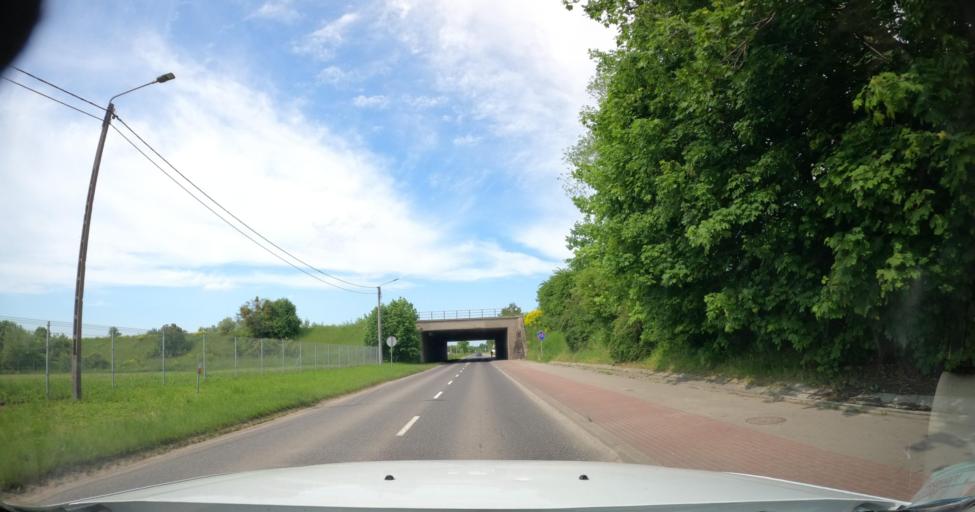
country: PL
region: Warmian-Masurian Voivodeship
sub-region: Powiat lidzbarski
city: Lidzbark Warminski
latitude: 54.1303
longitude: 20.5655
